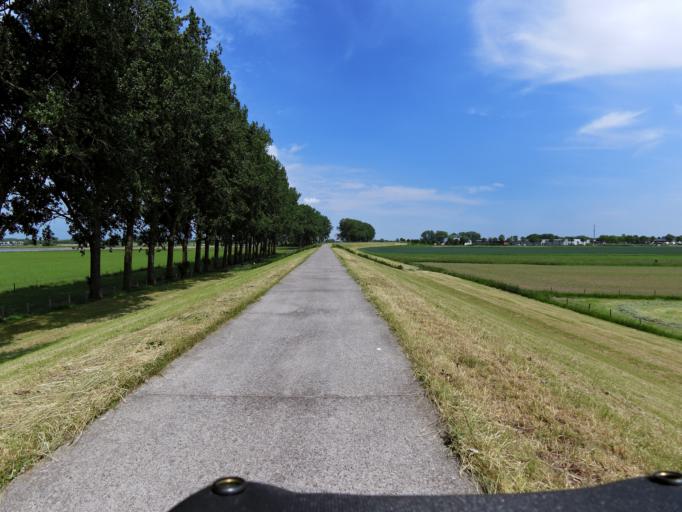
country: NL
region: North Brabant
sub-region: Gemeente Woudrichem
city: Woudrichem
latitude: 51.8172
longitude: 5.0721
